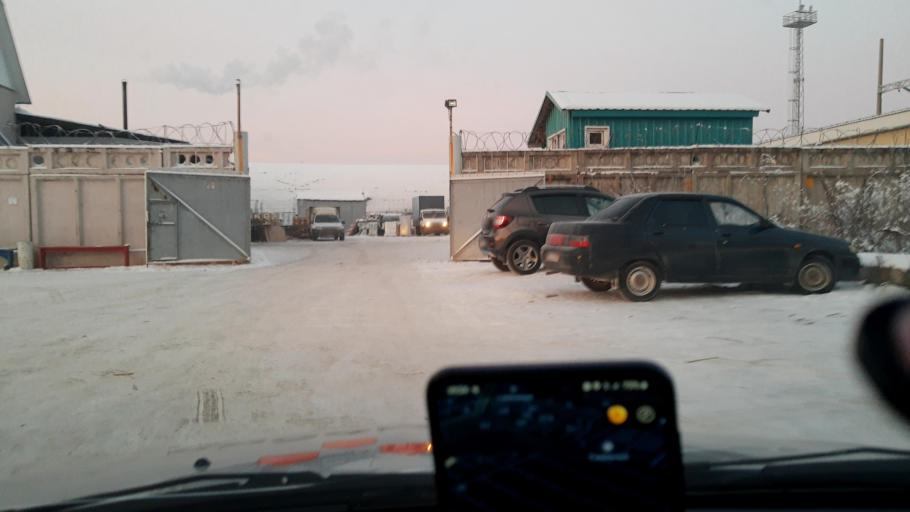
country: RU
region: Bashkortostan
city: Ufa
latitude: 54.8289
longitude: 56.1040
